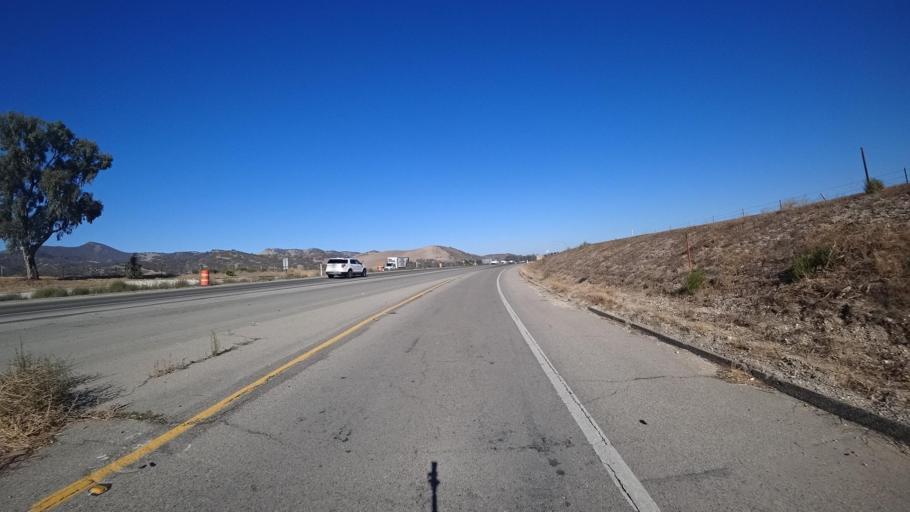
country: US
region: California
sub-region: Monterey County
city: King City
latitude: 36.1989
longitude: -121.1520
